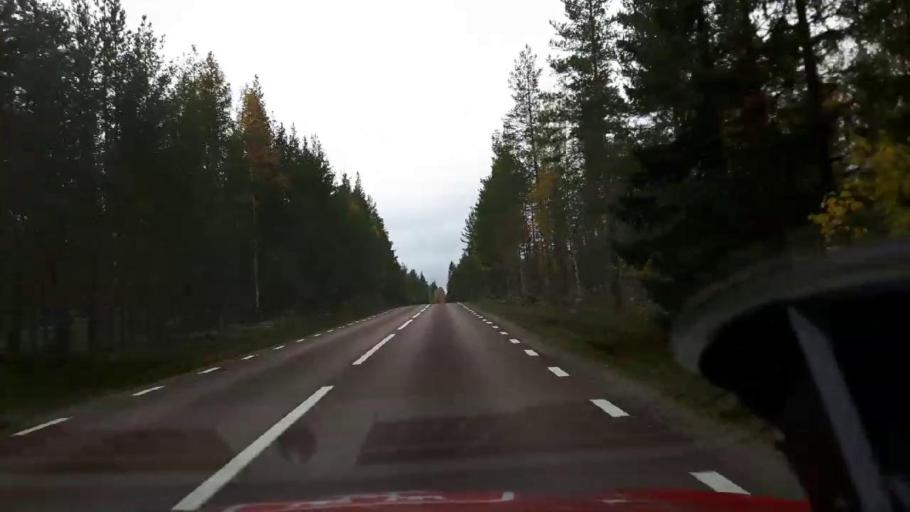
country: SE
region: Jaemtland
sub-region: Harjedalens Kommun
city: Sveg
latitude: 62.2184
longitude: 14.8479
